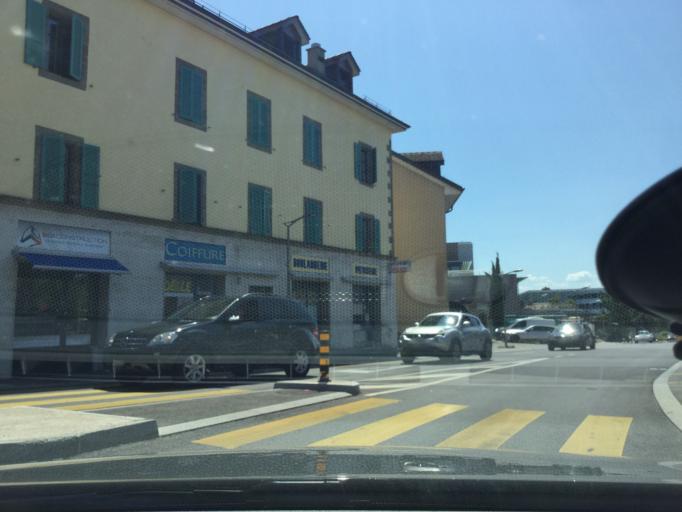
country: CH
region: Geneva
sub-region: Geneva
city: Vandoeuvres
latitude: 46.2398
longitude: 6.1981
